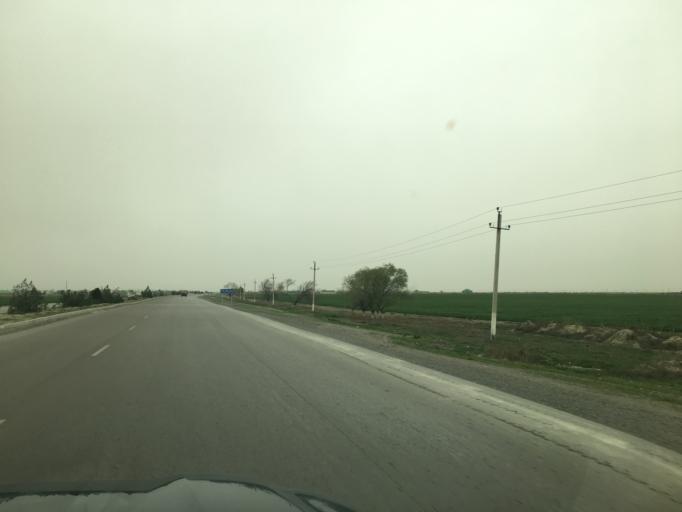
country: TM
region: Ahal
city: Baharly
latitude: 38.3903
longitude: 57.4869
